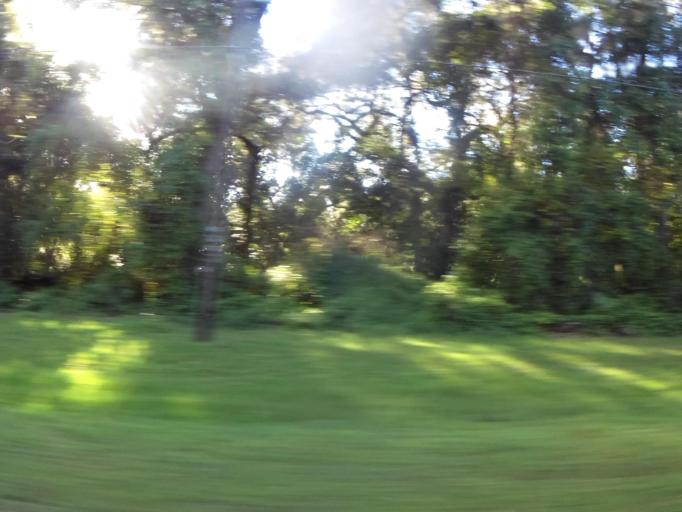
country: US
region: Florida
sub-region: Marion County
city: Citra
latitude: 29.4900
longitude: -82.1708
